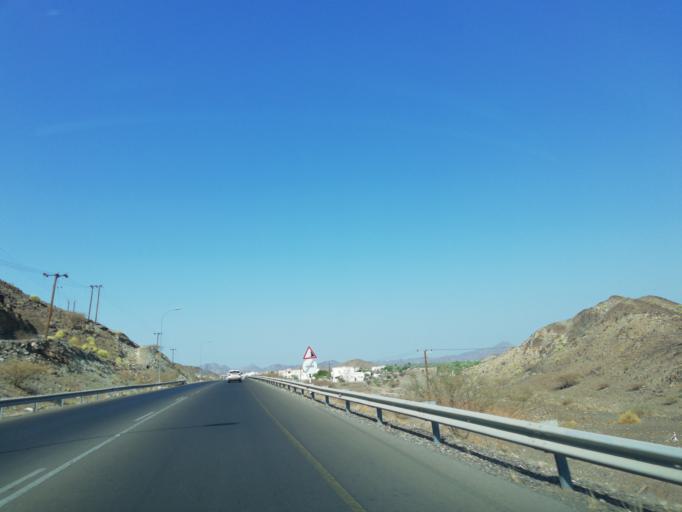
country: OM
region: Ash Sharqiyah
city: Ibra'
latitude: 22.8047
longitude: 58.1659
